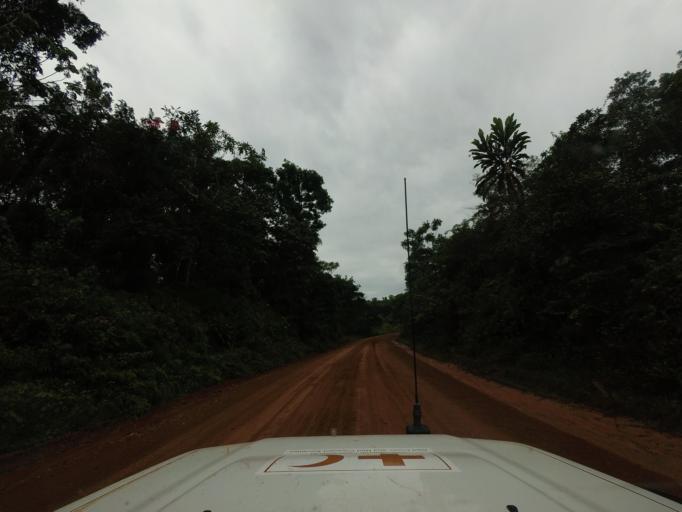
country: LR
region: Nimba
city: Sanniquellie
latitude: 7.4650
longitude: -8.6252
